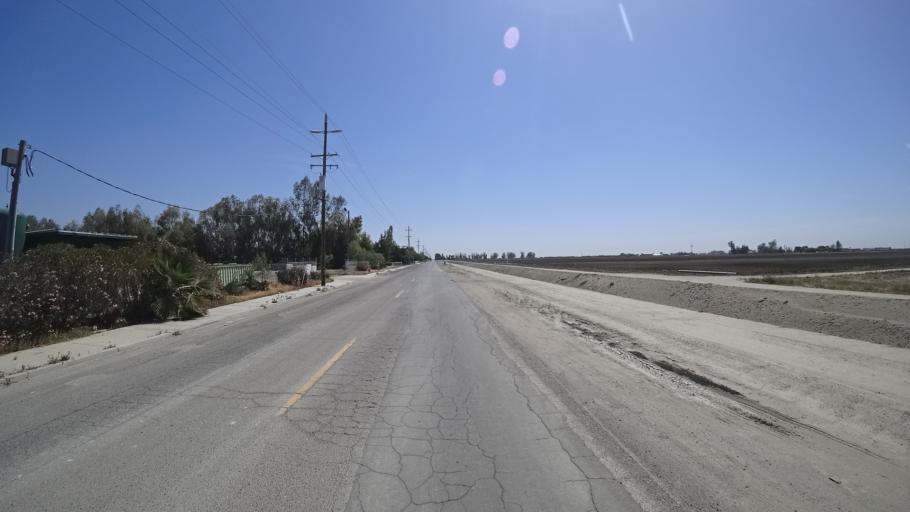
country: US
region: California
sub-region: Kings County
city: Corcoran
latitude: 36.0799
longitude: -119.5695
